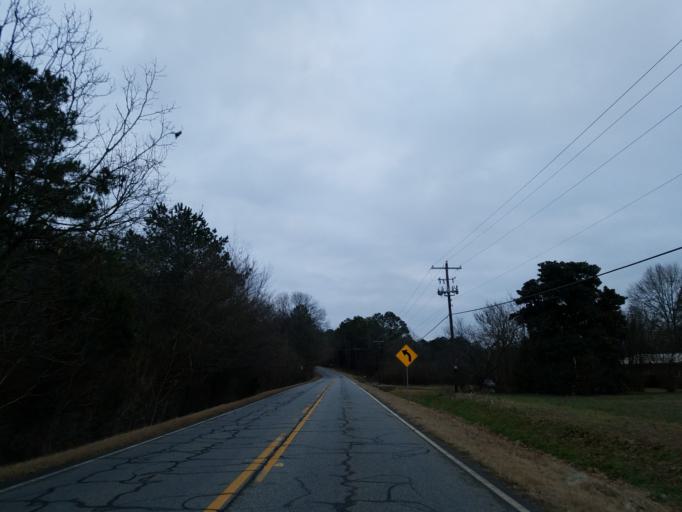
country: US
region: Georgia
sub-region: Bartow County
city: Cartersville
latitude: 34.2161
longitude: -84.8414
